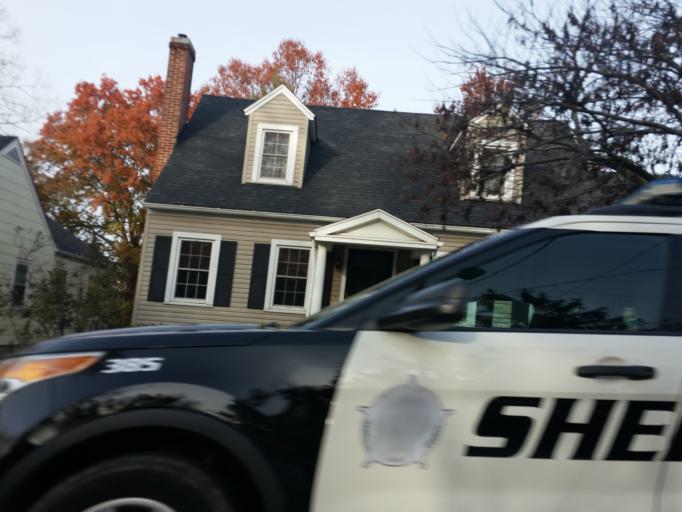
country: US
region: Kentucky
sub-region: Harrison County
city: Cynthiana
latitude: 38.3865
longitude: -84.2836
